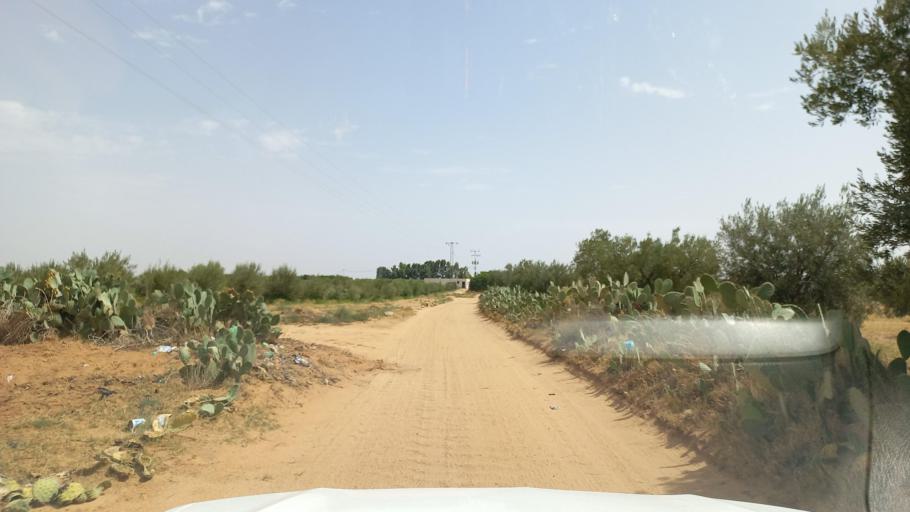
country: TN
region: Al Qasrayn
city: Kasserine
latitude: 35.2594
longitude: 9.0527
